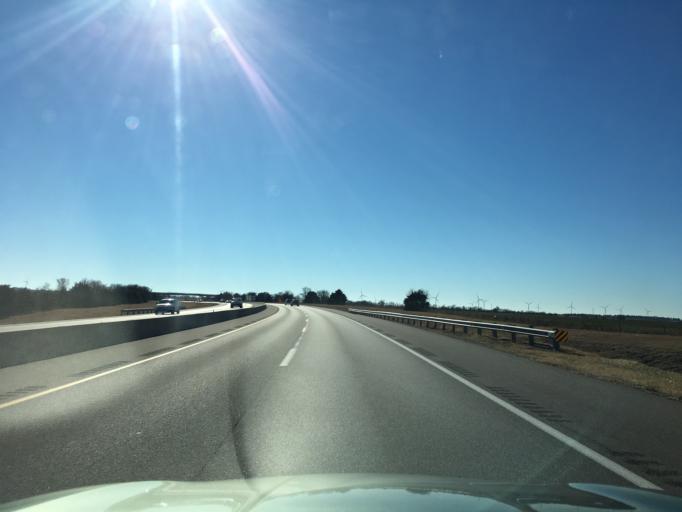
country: US
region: Kansas
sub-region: Sumner County
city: Wellington
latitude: 37.1940
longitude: -97.3416
